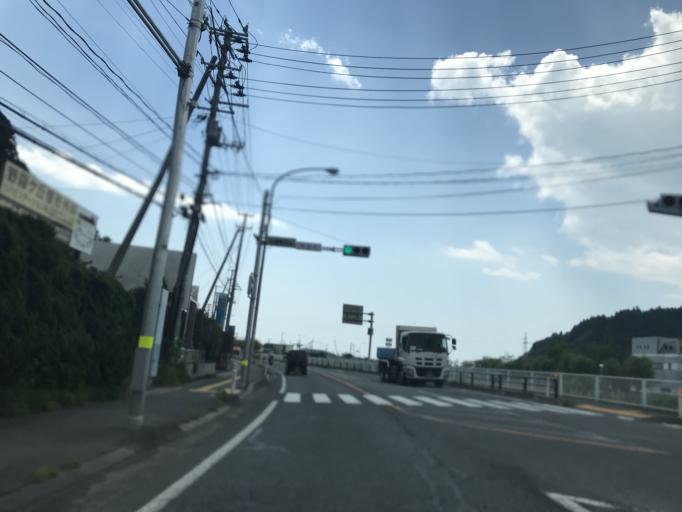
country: JP
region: Miyagi
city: Matsushima
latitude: 38.3933
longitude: 141.0672
